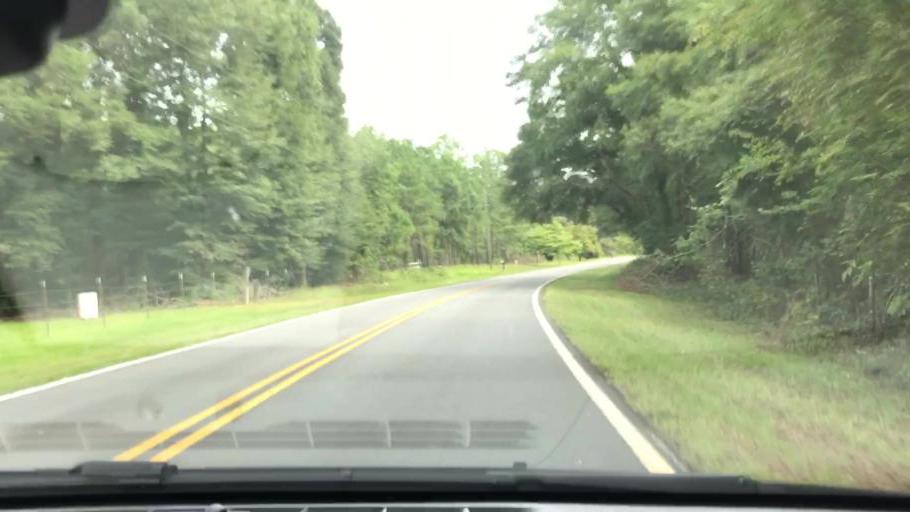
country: US
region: Georgia
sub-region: Clay County
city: Fort Gaines
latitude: 31.5495
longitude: -84.9670
